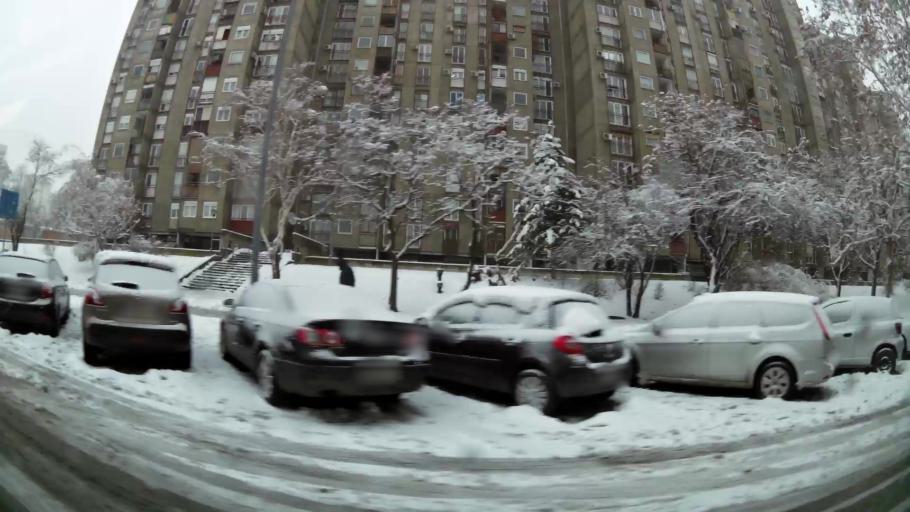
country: RS
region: Central Serbia
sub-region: Belgrade
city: Novi Beograd
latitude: 44.8040
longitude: 20.3797
